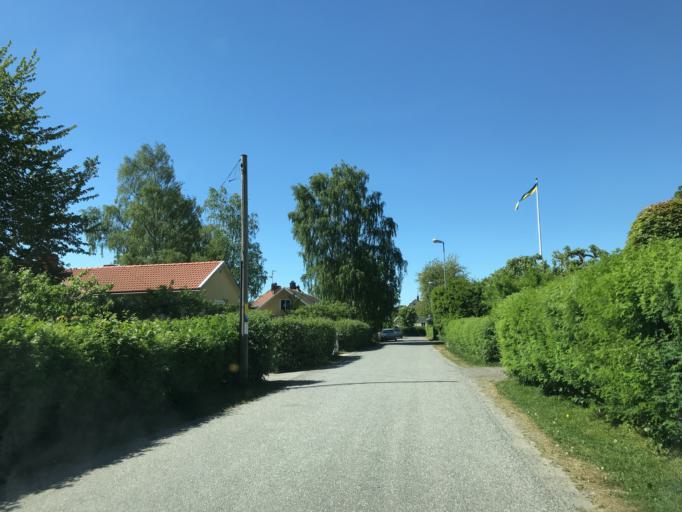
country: SE
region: Stockholm
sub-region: Sollentuna Kommun
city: Sollentuna
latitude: 59.4220
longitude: 17.9614
